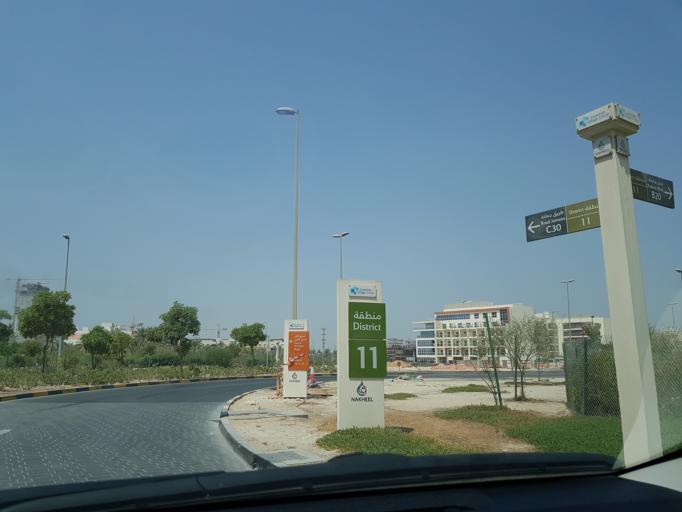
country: AE
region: Dubai
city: Dubai
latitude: 25.0581
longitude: 55.2086
